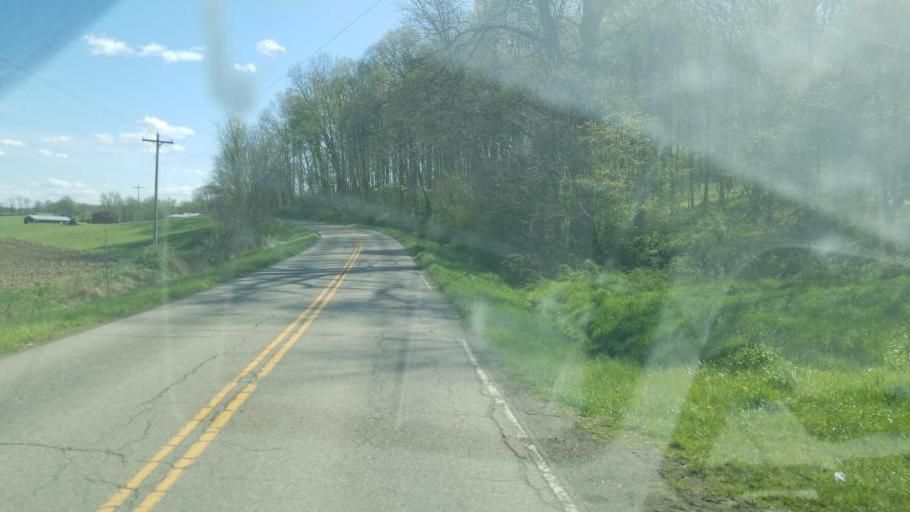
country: US
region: Ohio
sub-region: Coshocton County
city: Coshocton
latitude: 40.3839
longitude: -81.8511
